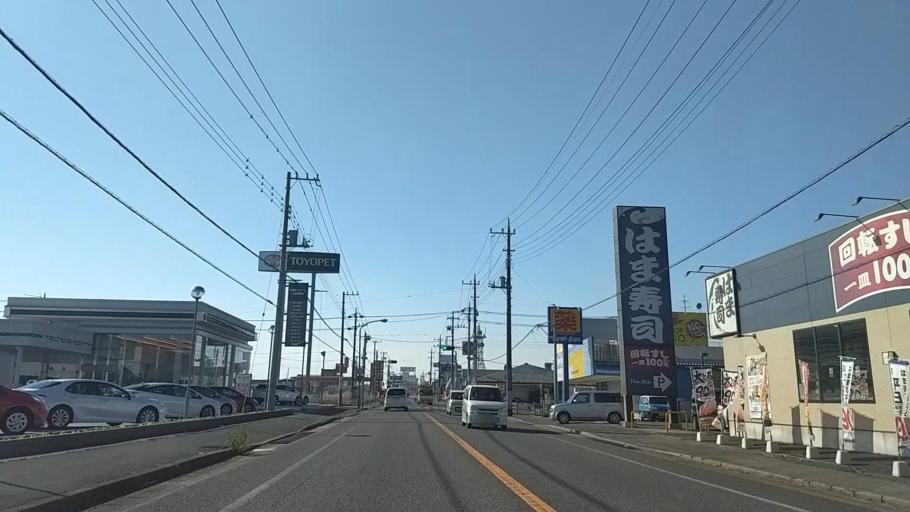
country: JP
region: Chiba
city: Yokaichiba
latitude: 35.7048
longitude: 140.5602
